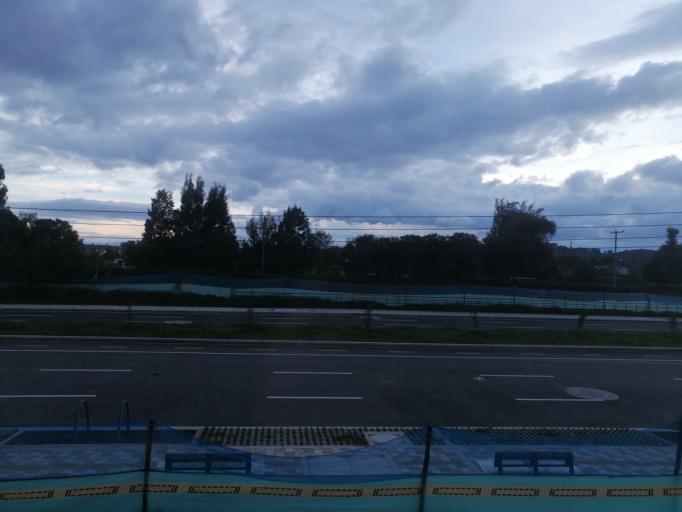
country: CO
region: Cundinamarca
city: Cota
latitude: 4.7648
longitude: -74.0517
